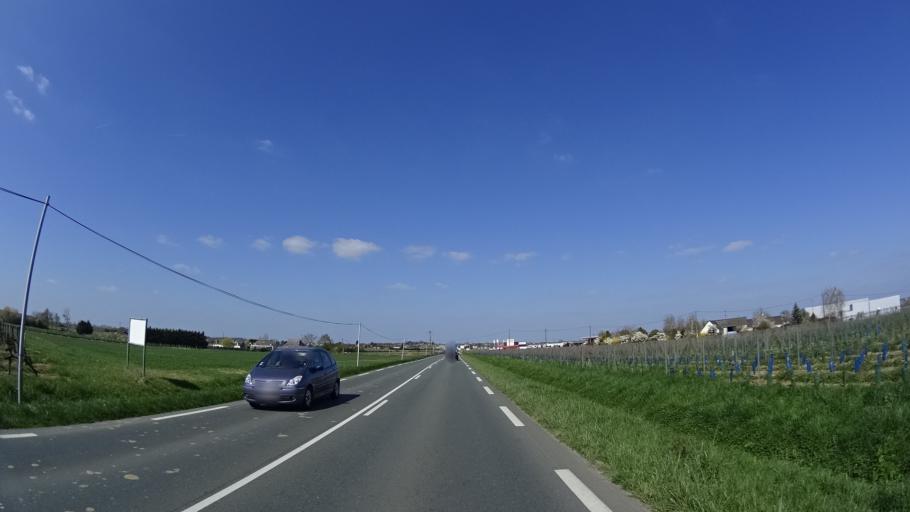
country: FR
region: Pays de la Loire
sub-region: Departement de Maine-et-Loire
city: Brissac-Quince
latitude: 47.3373
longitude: -0.4296
